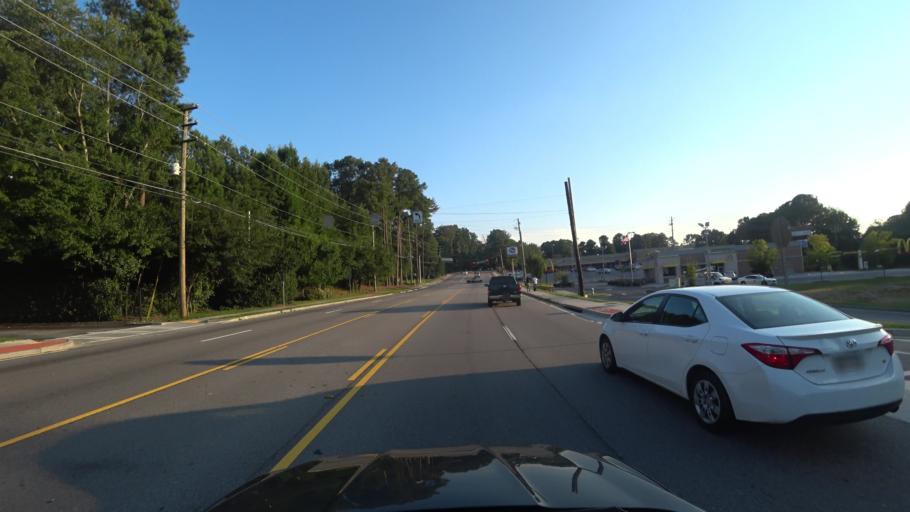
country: US
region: Georgia
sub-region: DeKalb County
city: North Atlanta
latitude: 33.8573
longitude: -84.3119
